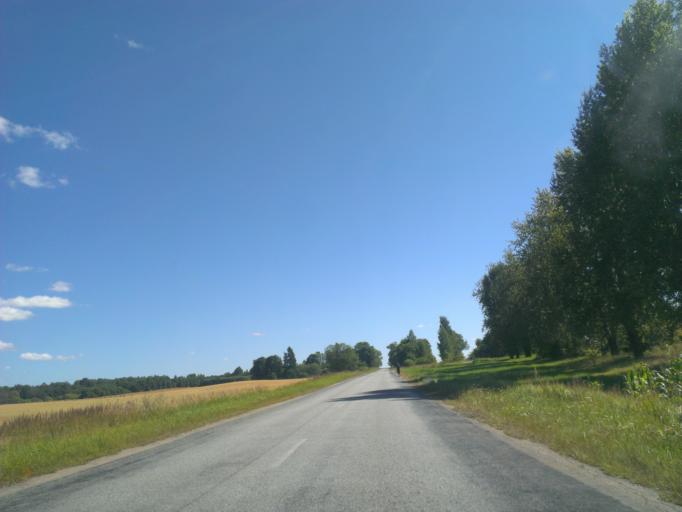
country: LV
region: Malpils
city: Malpils
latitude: 57.0232
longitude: 24.8392
